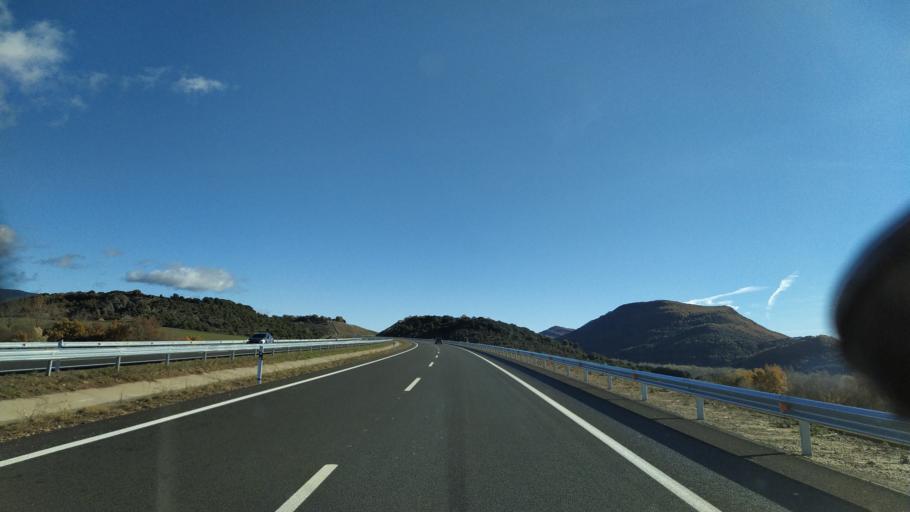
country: ES
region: Aragon
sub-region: Provincia de Huesca
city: Santa Cruz de la Seros
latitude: 42.5634
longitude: -0.6929
